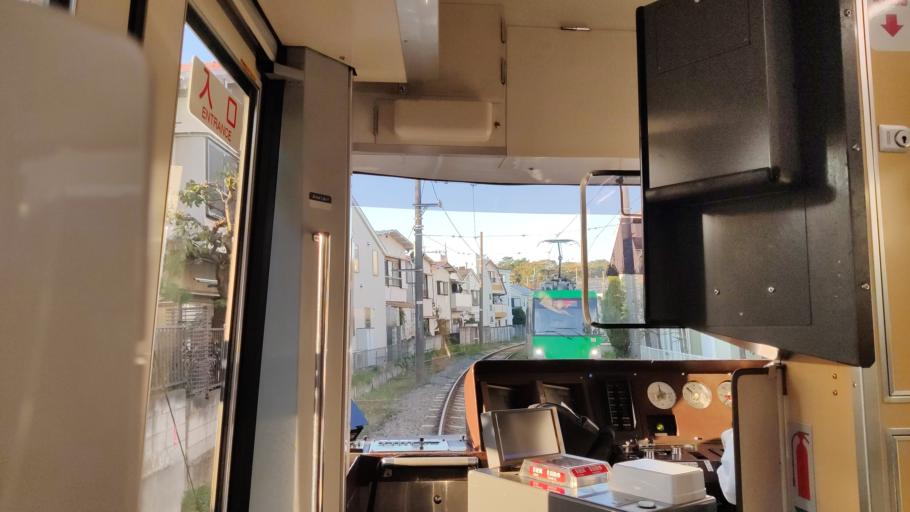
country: JP
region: Tokyo
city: Tokyo
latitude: 35.6460
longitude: 139.6449
